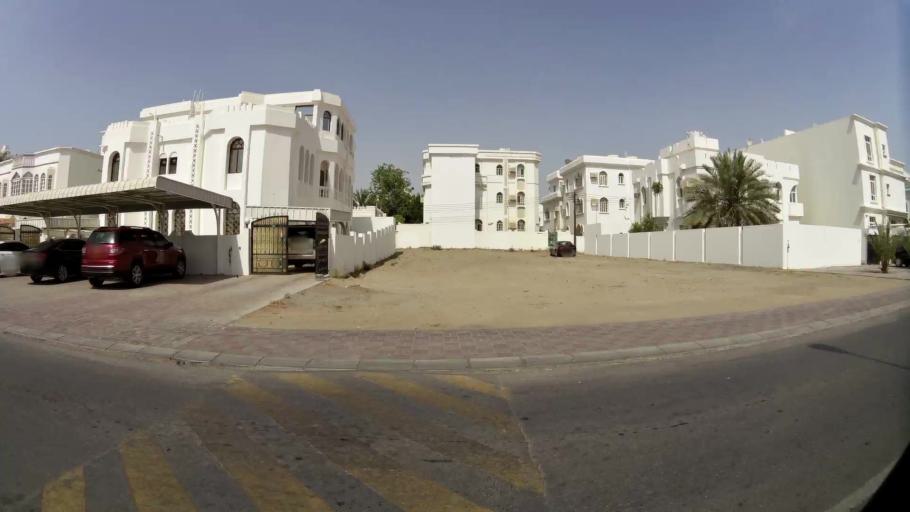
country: OM
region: Muhafazat Masqat
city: Bawshar
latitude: 23.5786
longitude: 58.4027
